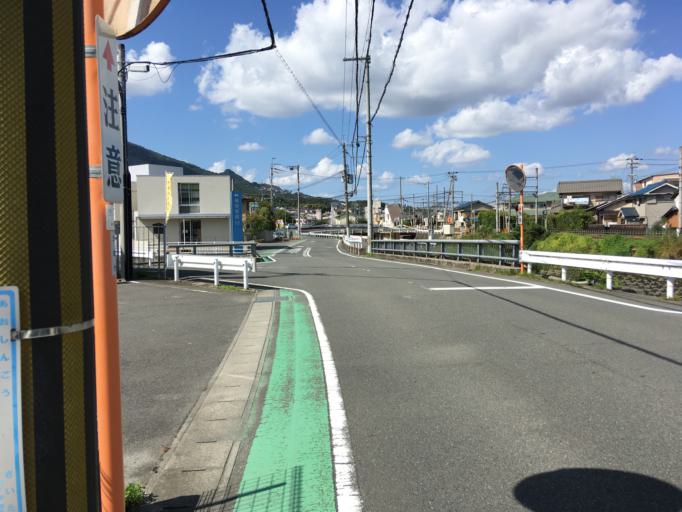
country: JP
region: Nara
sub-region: Ikoma-shi
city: Ikoma
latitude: 34.6634
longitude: 135.7101
